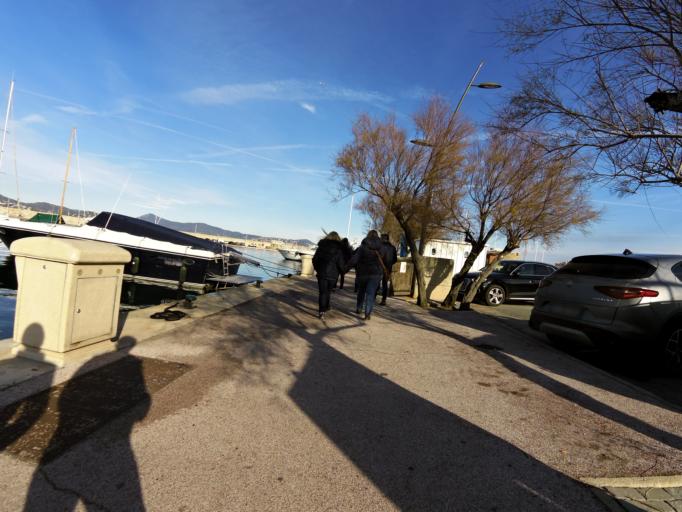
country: FR
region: Provence-Alpes-Cote d'Azur
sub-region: Departement du Var
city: Saint-Tropez
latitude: 43.2717
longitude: 6.6344
